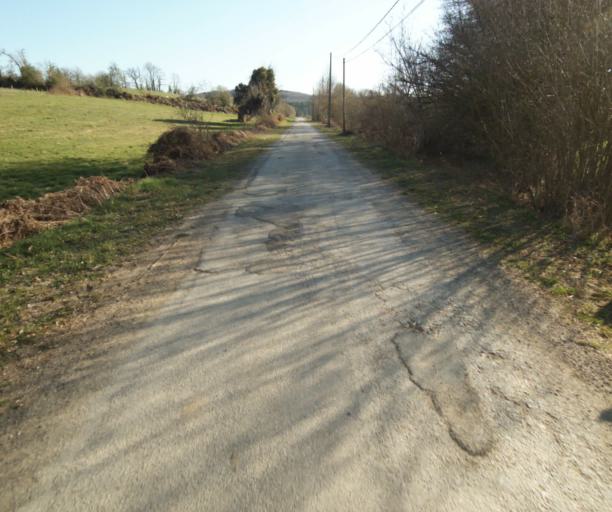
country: FR
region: Limousin
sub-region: Departement de la Correze
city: Chamboulive
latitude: 45.5007
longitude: 1.7255
